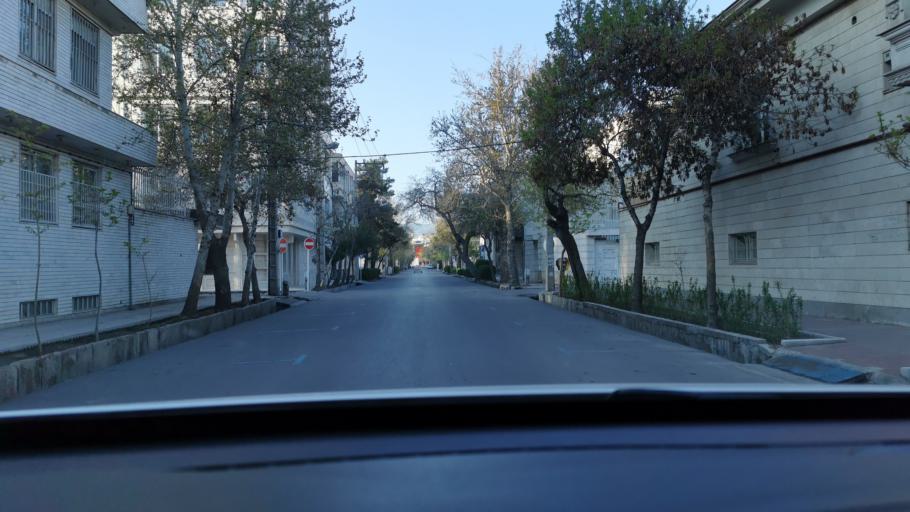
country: IR
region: Razavi Khorasan
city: Mashhad
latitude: 36.2976
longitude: 59.5798
